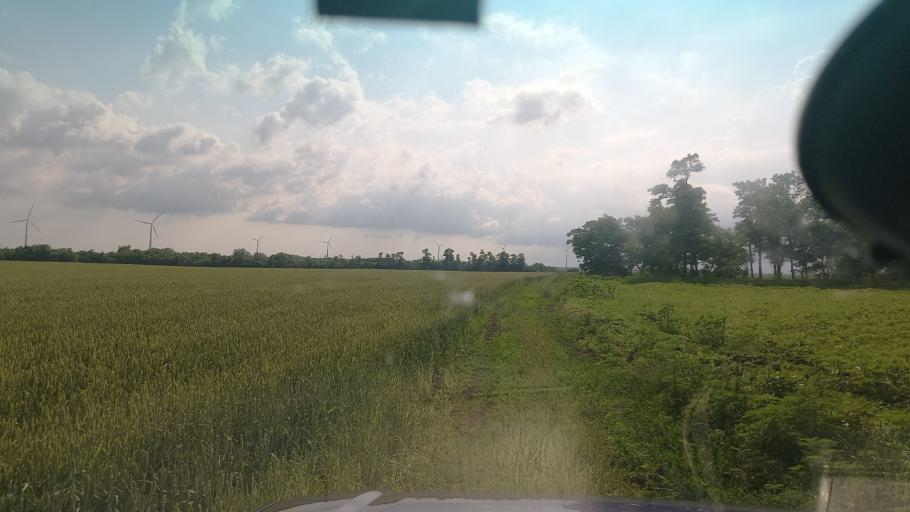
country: RU
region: Adygeya
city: Giaginskaya
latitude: 44.9572
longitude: 40.1145
